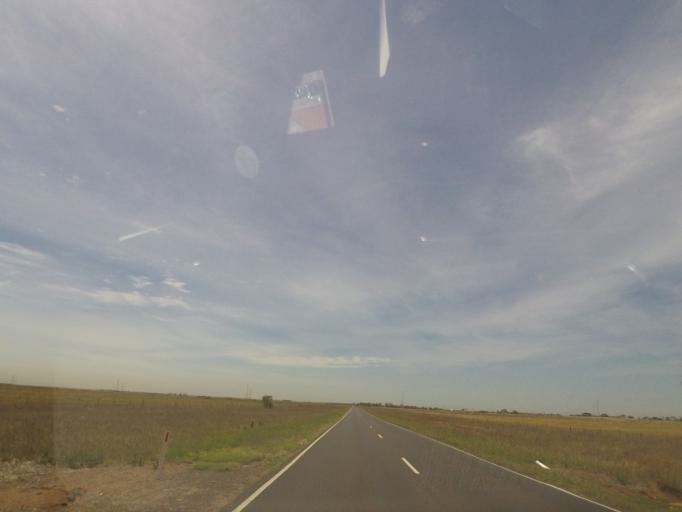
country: AU
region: Victoria
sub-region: Wyndham
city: Wyndham Vale
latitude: -37.8239
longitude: 144.5336
